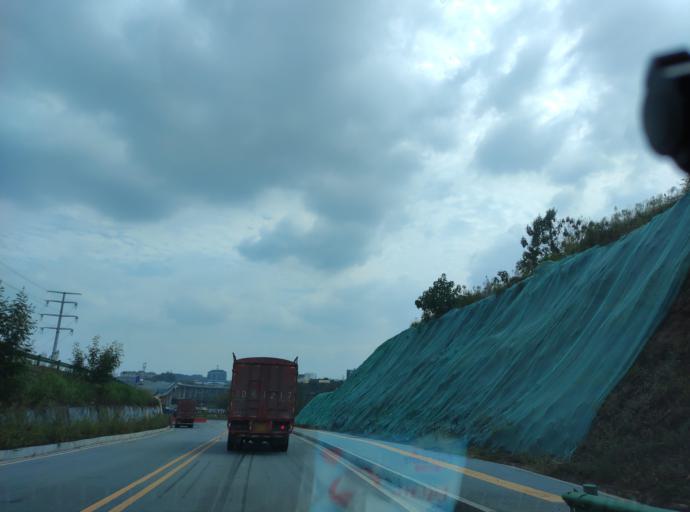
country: CN
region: Jiangxi Sheng
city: Pingxiang
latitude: 27.6629
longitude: 113.9080
